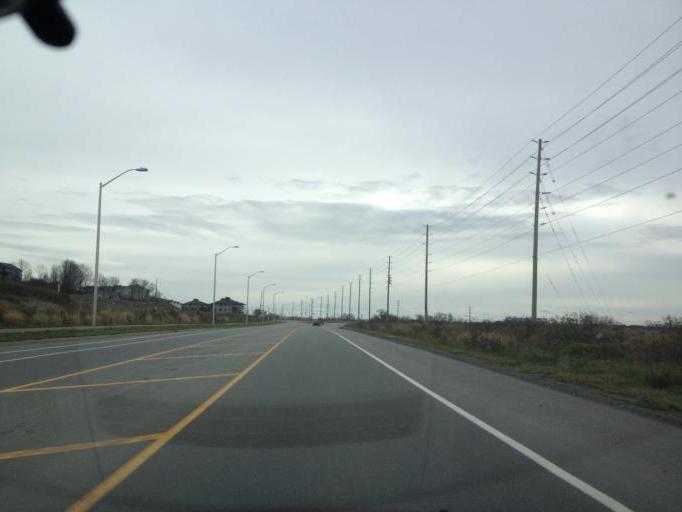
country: CA
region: Ontario
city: Bells Corners
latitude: 45.3168
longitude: -75.9432
